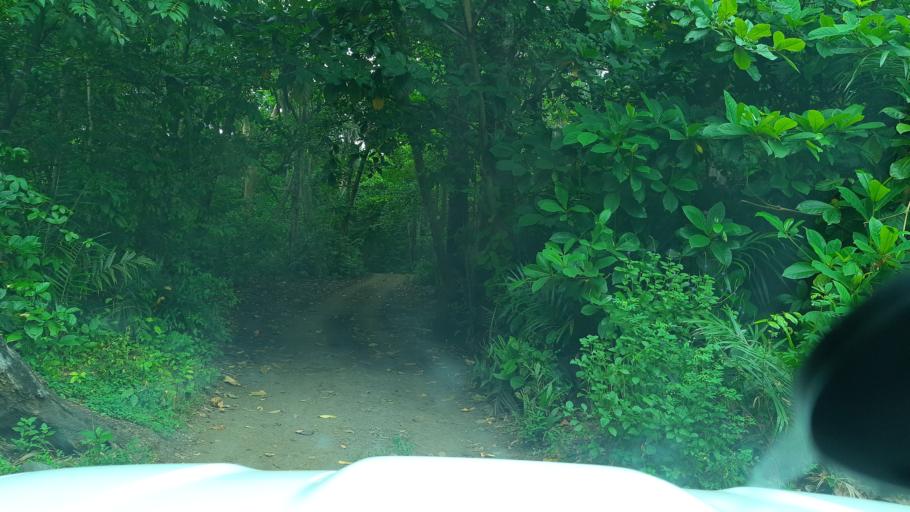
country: ST
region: Sao Tome Island
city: Sao Tome
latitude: 0.2453
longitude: 6.7453
